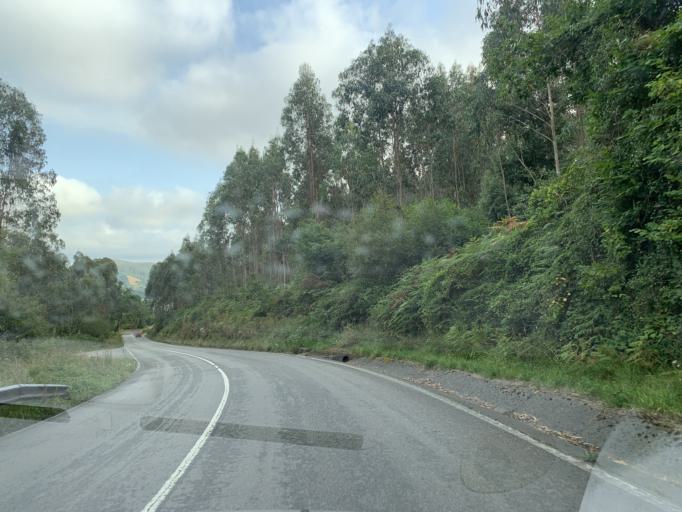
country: ES
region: Asturias
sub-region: Province of Asturias
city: Villaviciosa
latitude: 43.5144
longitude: -5.4275
